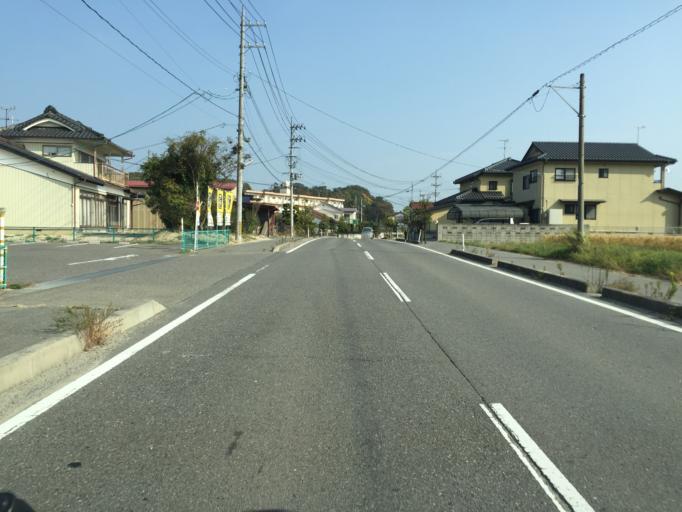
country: JP
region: Fukushima
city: Koriyama
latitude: 37.4577
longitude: 140.3839
